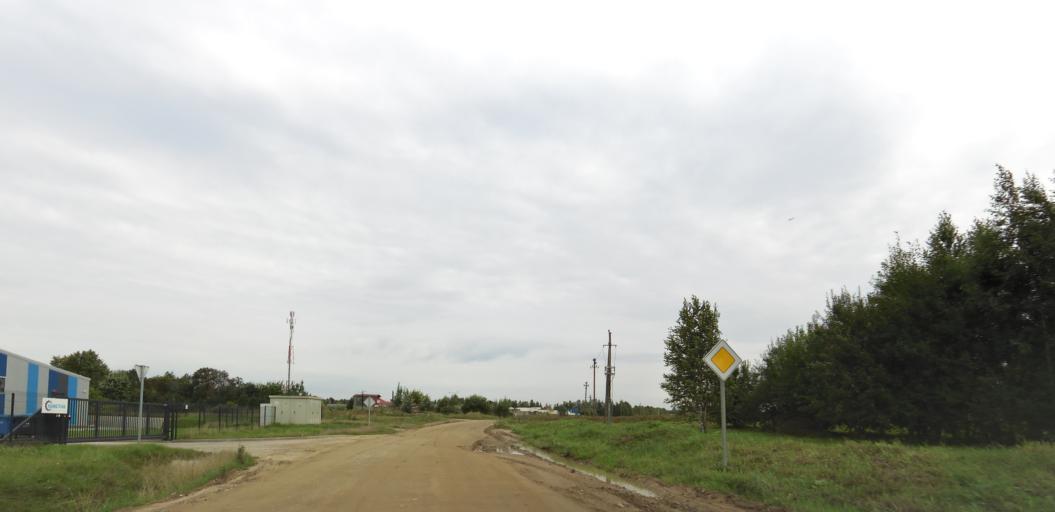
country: LT
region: Vilnius County
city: Pasilaiciai
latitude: 54.7557
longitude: 25.2181
